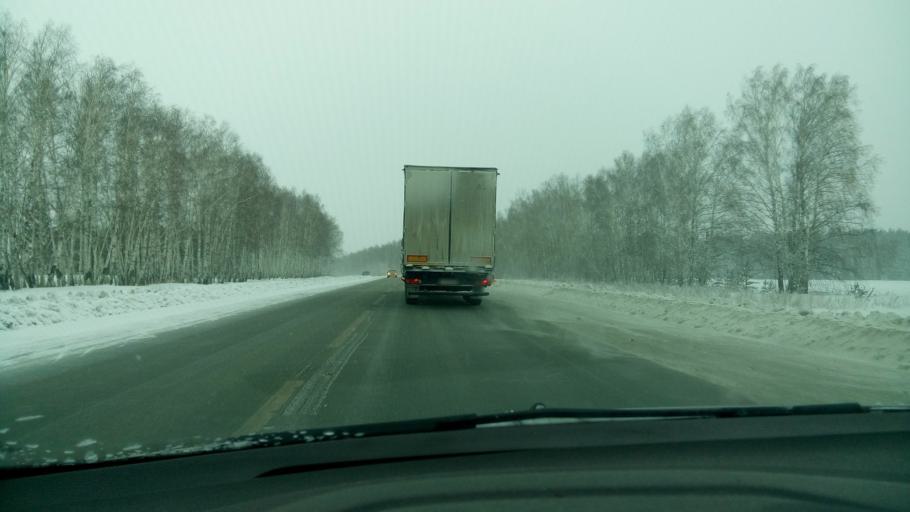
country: RU
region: Sverdlovsk
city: Zarechnyy
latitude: 56.7477
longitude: 61.3027
